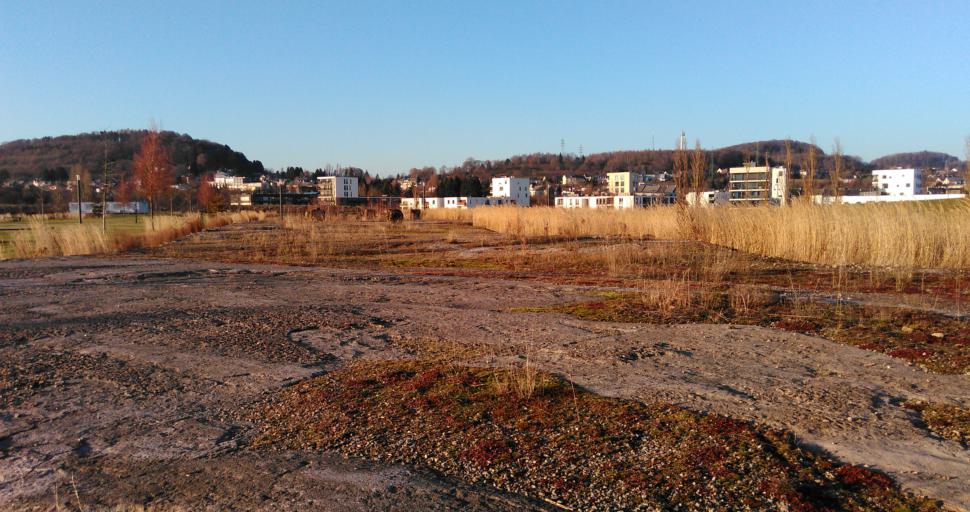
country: LU
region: Luxembourg
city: Belvaux
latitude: 49.5055
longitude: 5.9384
